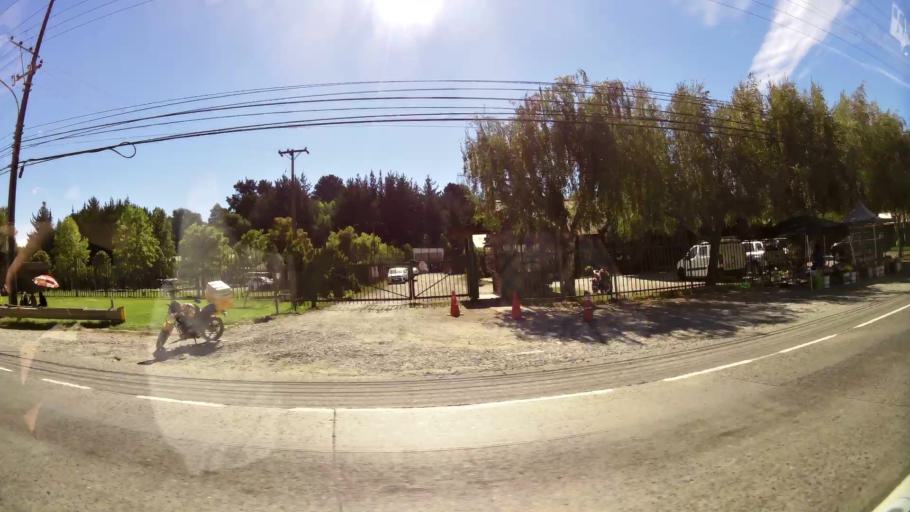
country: CL
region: Biobio
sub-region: Provincia de Concepcion
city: Penco
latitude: -36.7733
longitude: -73.0156
